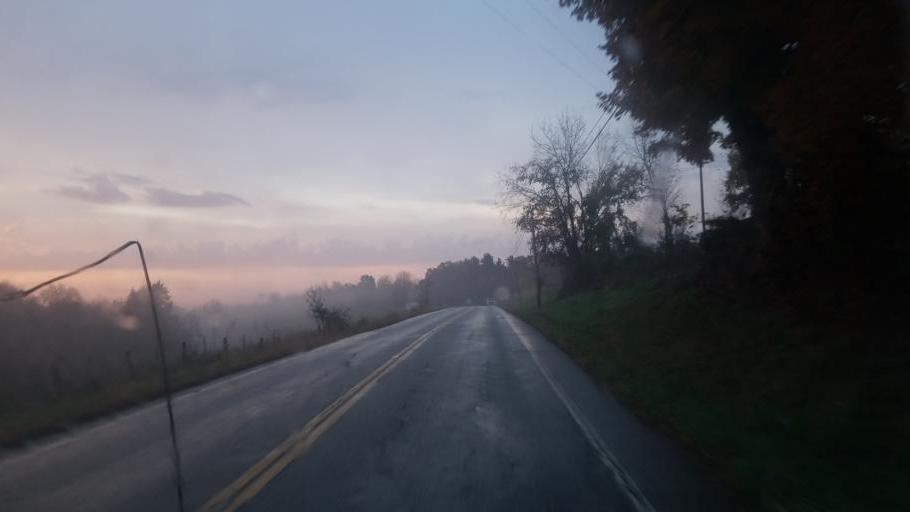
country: US
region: Ohio
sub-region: Morgan County
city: McConnelsville
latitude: 39.5202
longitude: -81.8507
